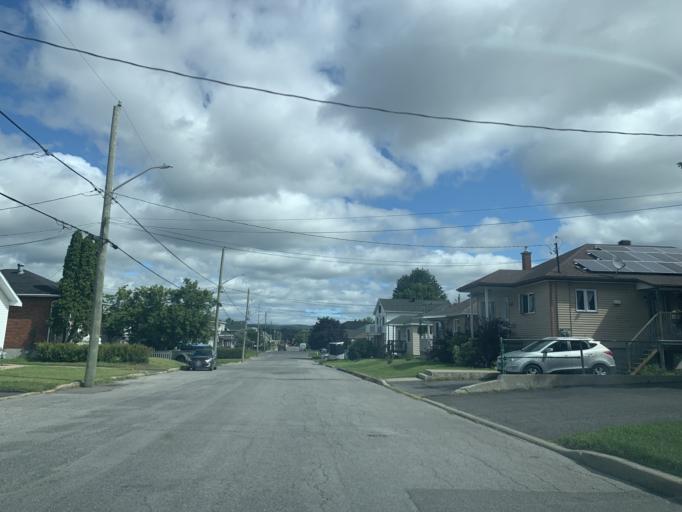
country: CA
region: Ontario
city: Hawkesbury
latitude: 45.6054
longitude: -74.5930
